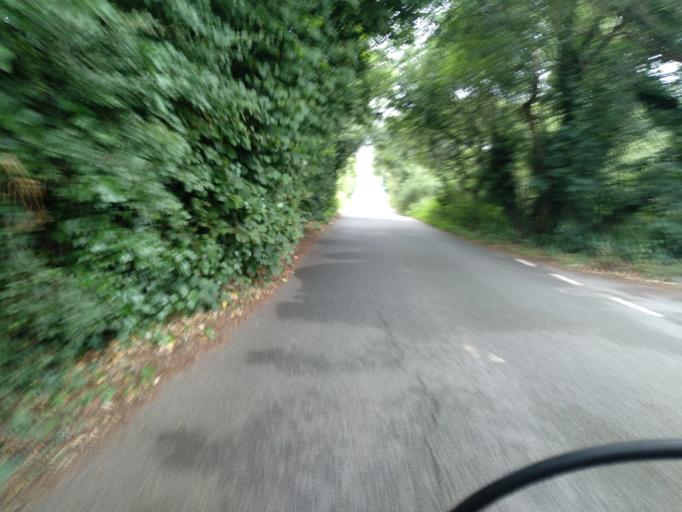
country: GB
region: England
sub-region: Isle of Wight
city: Sandown
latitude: 50.6607
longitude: -1.1673
